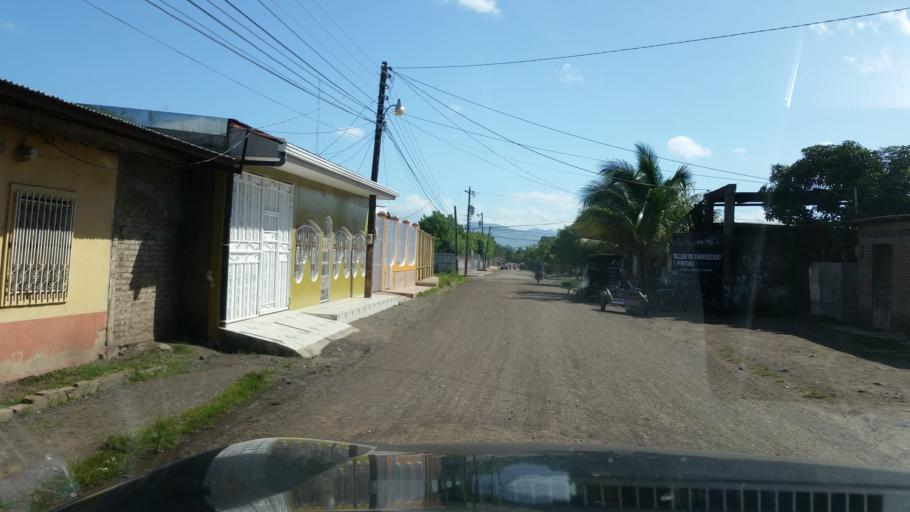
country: NI
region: Matagalpa
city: Ciudad Dario
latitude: 12.8577
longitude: -86.0941
